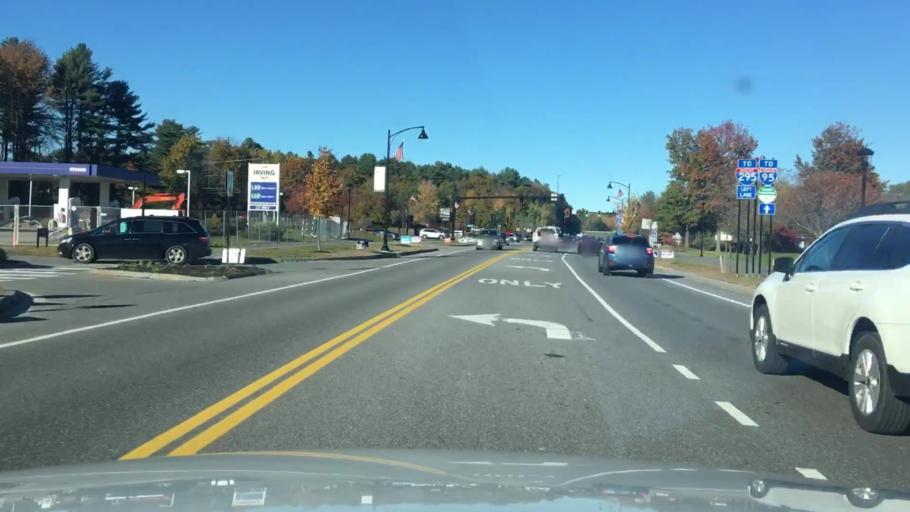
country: US
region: Maine
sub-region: Cumberland County
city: Falmouth
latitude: 43.7246
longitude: -70.2321
